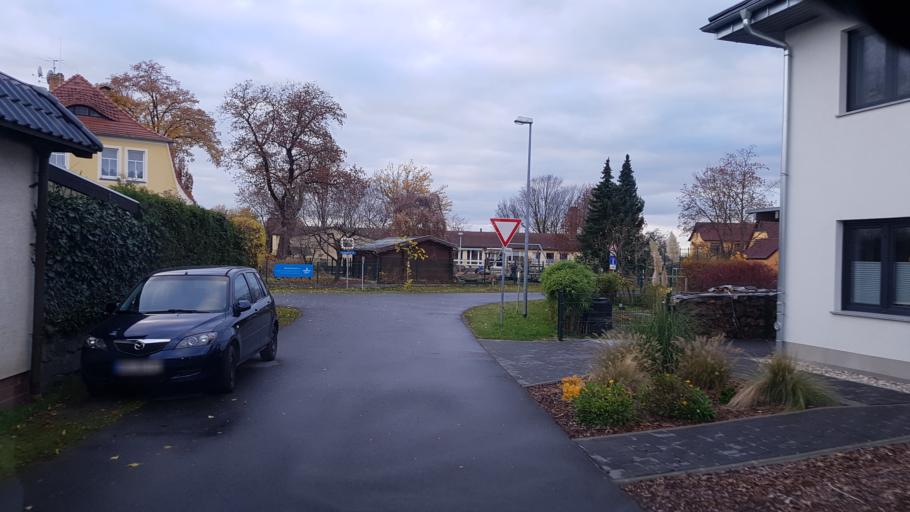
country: DE
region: Brandenburg
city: Kroppen
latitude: 51.3848
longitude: 13.7933
